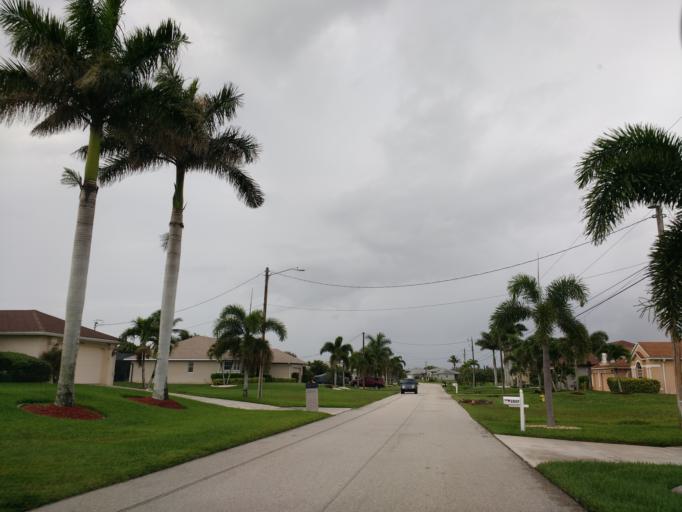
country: US
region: Florida
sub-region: Lee County
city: Cape Coral
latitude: 26.5979
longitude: -82.0234
